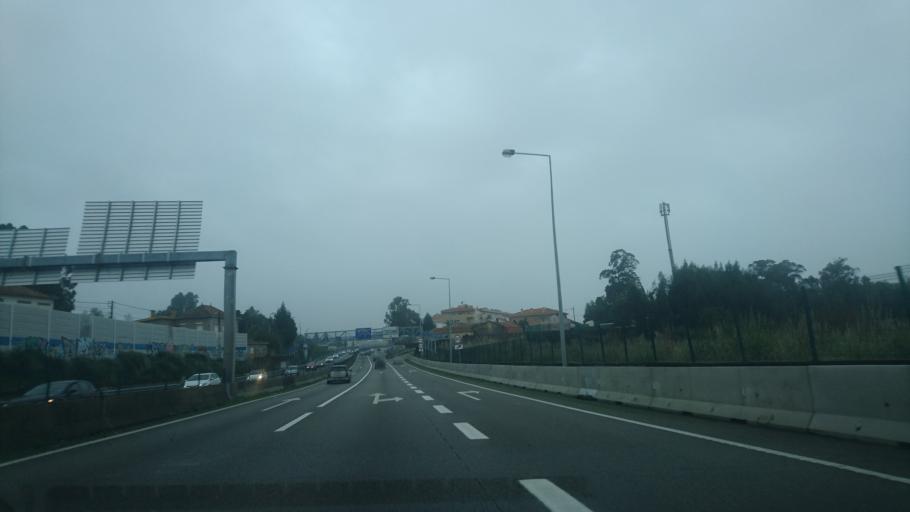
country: PT
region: Porto
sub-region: Vila Nova de Gaia
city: Vilar do Paraiso
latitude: 41.1043
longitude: -8.6265
